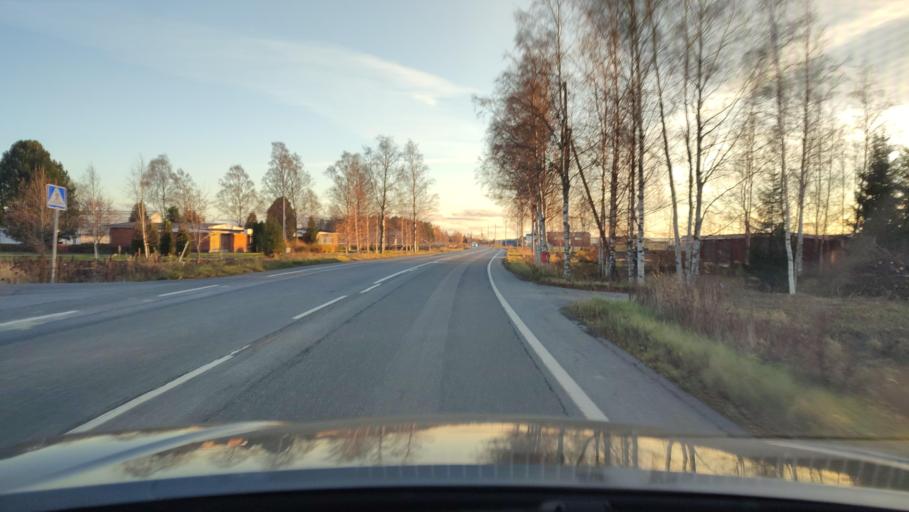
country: FI
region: Ostrobothnia
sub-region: Sydosterbotten
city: Naerpes
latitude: 62.4510
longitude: 21.3529
